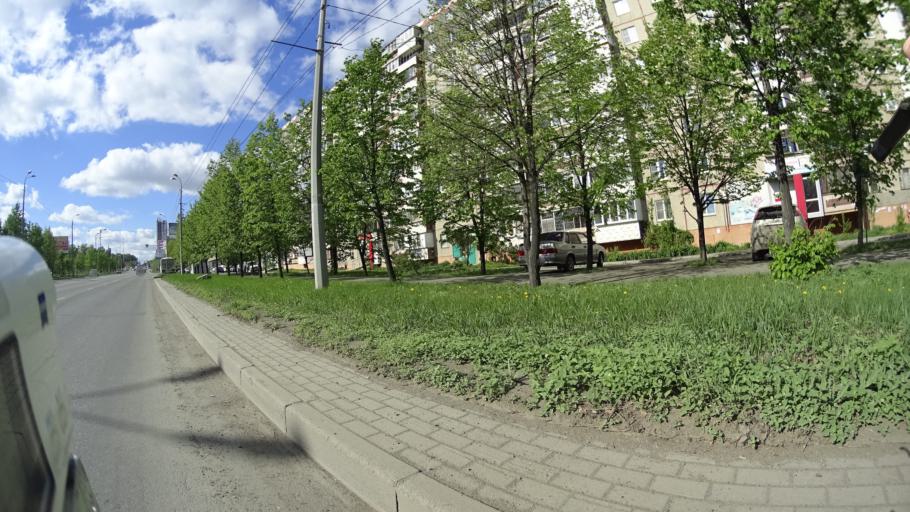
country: RU
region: Chelyabinsk
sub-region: Gorod Chelyabinsk
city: Chelyabinsk
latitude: 55.1718
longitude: 61.2942
